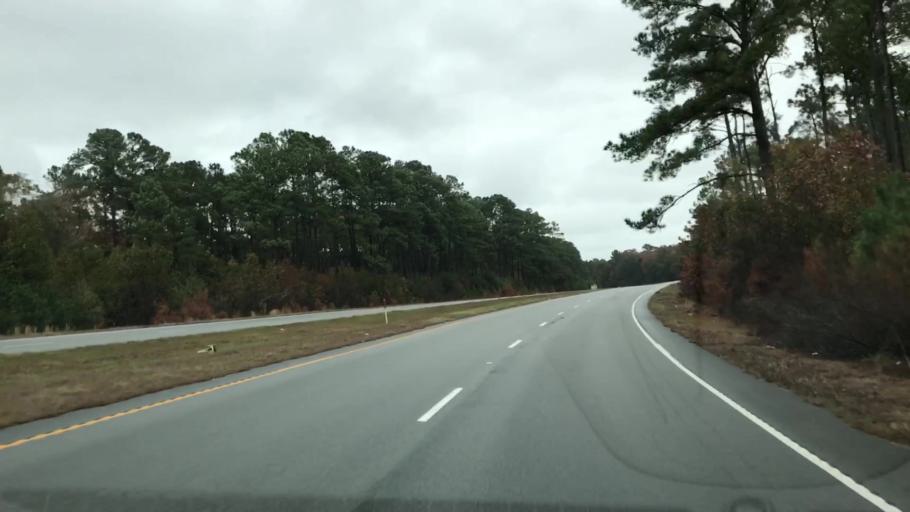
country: US
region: South Carolina
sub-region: Georgetown County
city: Georgetown
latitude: 33.1805
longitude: -79.4118
